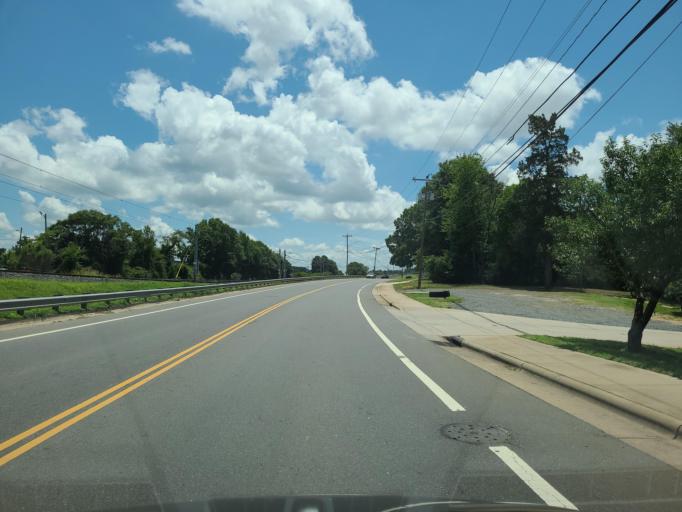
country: US
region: North Carolina
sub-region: Mecklenburg County
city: Pineville
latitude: 35.1571
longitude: -80.8772
